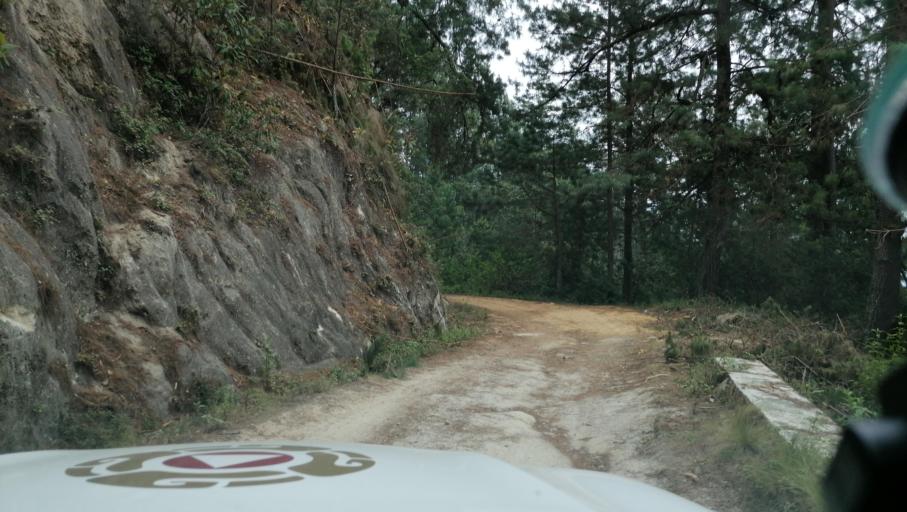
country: MX
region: Chiapas
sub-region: Tapachula
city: Canton Villaflor
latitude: 15.1992
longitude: -92.2340
